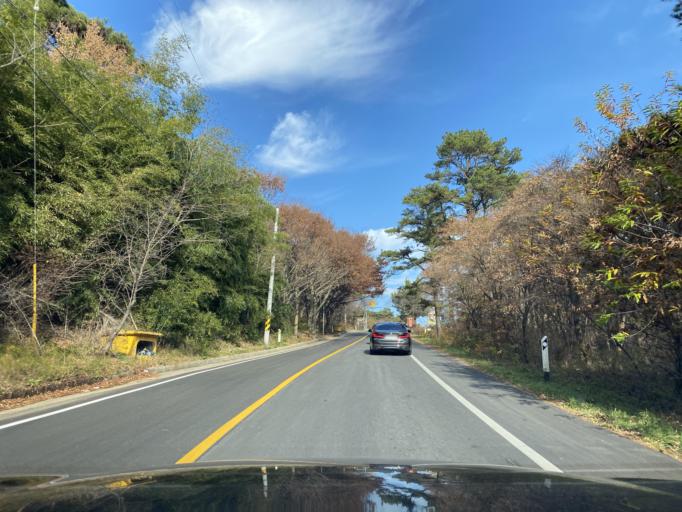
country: KR
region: Chungcheongnam-do
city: Hongsung
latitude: 36.6604
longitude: 126.6295
